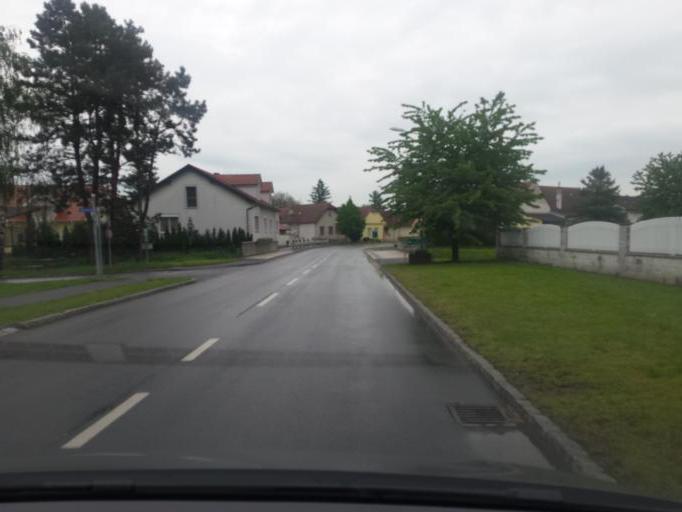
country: AT
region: Burgenland
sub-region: Politischer Bezirk Oberpullendorf
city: Lutzmannsburg
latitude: 47.4543
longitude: 16.6133
